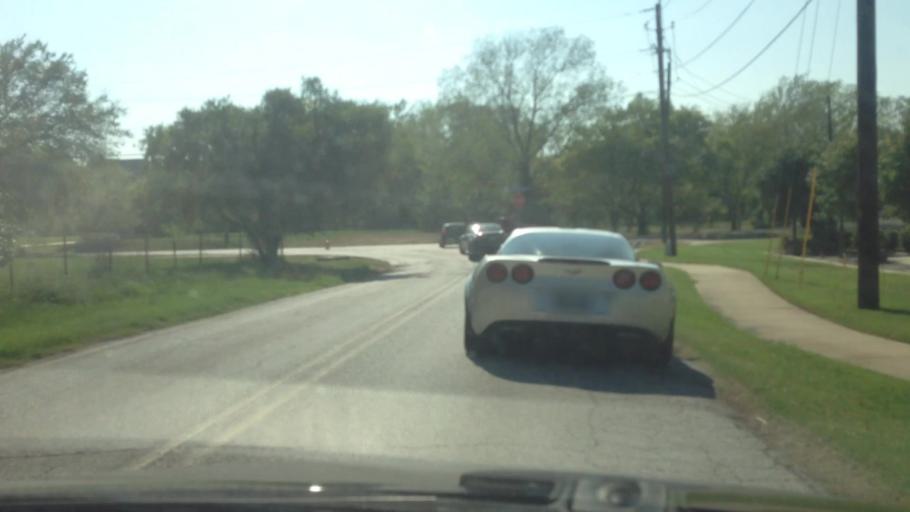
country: US
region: Texas
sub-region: Tarrant County
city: Colleyville
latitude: 32.9004
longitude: -97.1539
